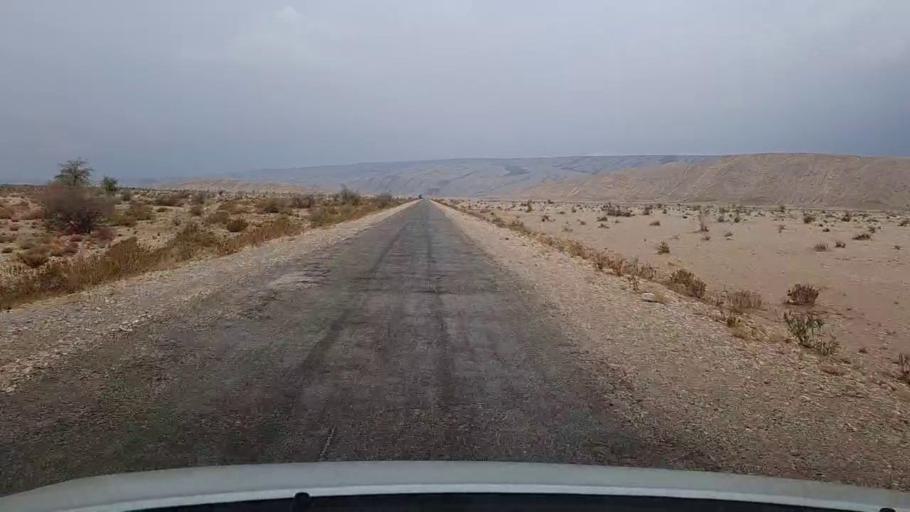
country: PK
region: Sindh
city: Sehwan
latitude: 26.2473
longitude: 67.7168
